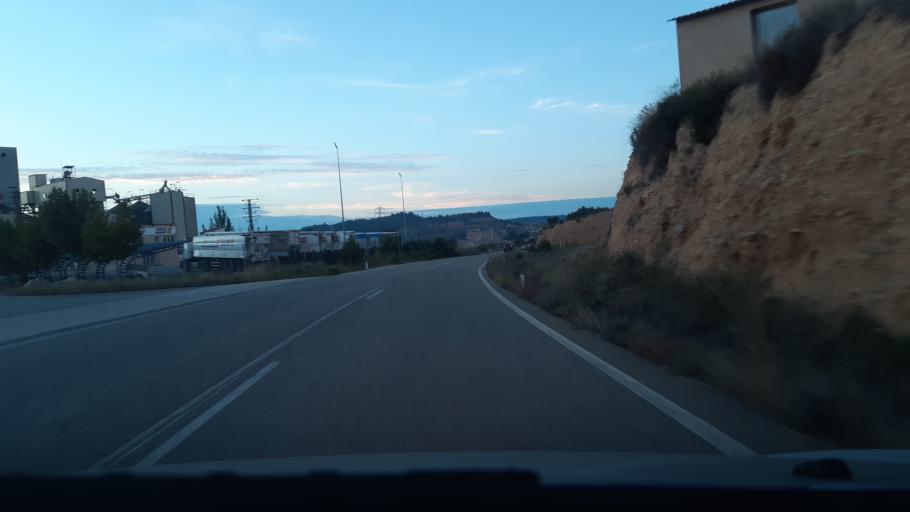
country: ES
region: Aragon
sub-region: Provincia de Teruel
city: Valderrobres
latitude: 40.8653
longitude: 0.1638
